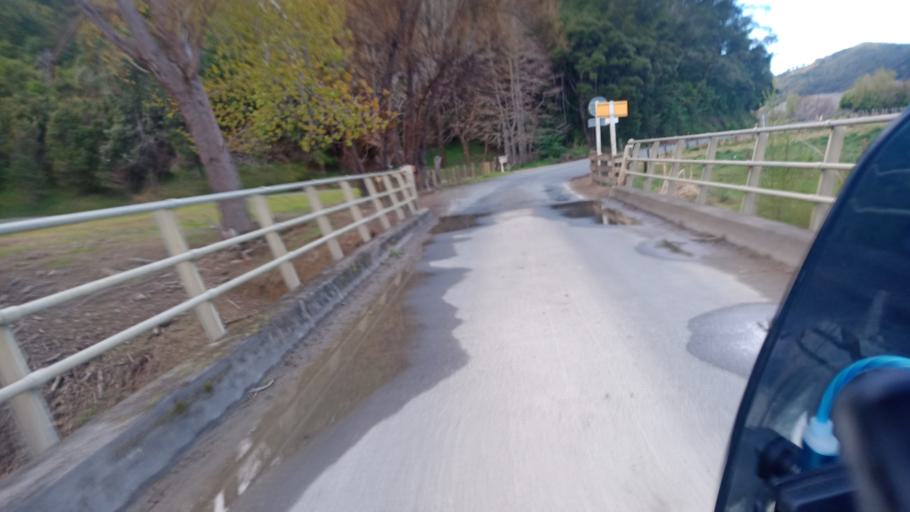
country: NZ
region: Gisborne
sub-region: Gisborne District
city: Gisborne
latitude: -38.2993
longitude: 178.2587
